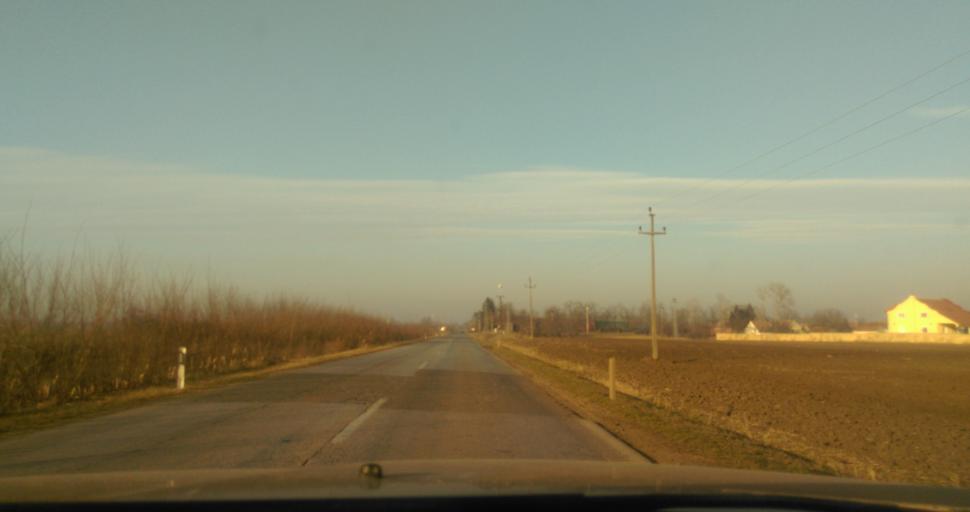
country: RS
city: Backo Gradiste
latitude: 45.5154
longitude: 20.0263
